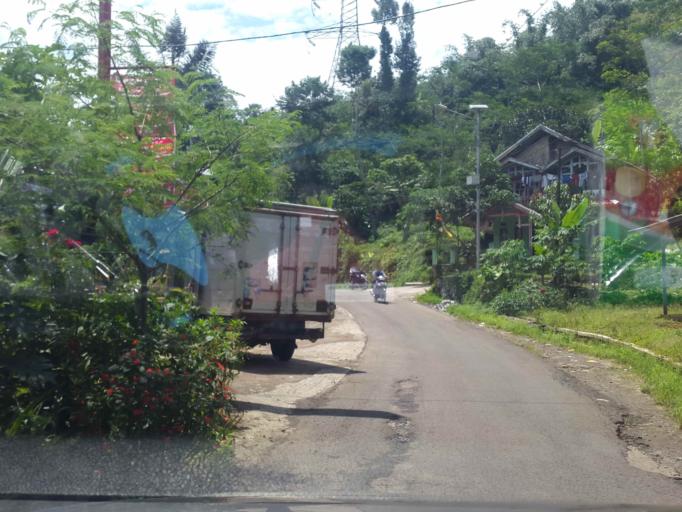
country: ID
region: West Java
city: Kupel
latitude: -7.0745
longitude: 107.1740
